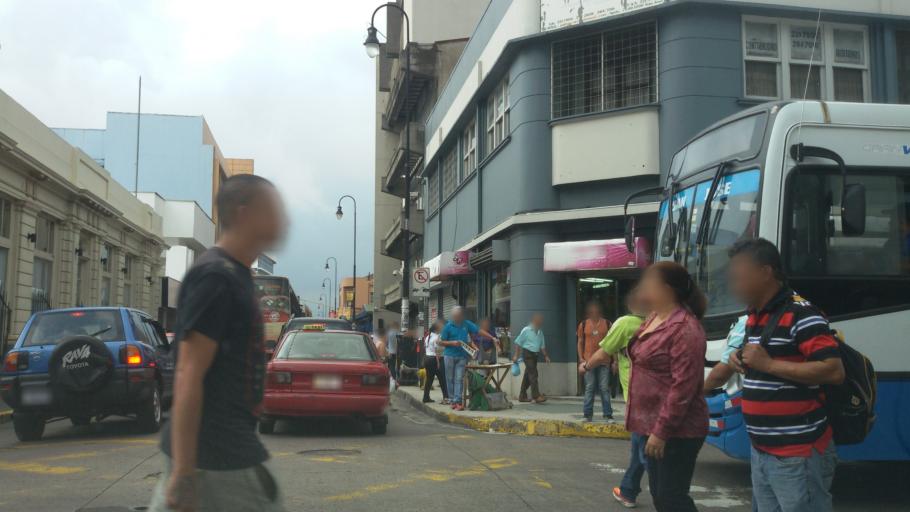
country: CR
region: San Jose
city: San Jose
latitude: 9.9357
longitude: -84.0790
